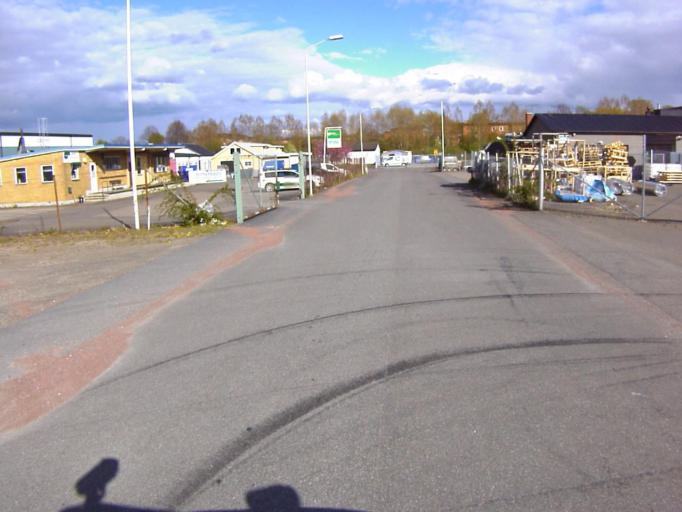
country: SE
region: Skane
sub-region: Kristianstads Kommun
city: Kristianstad
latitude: 56.0480
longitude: 14.1625
